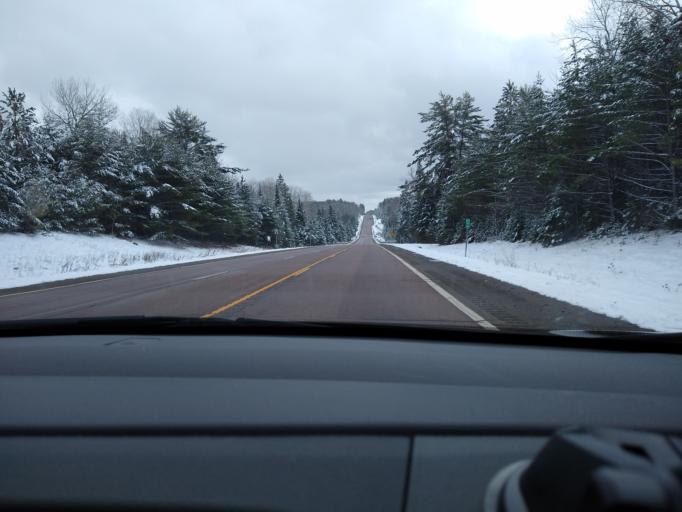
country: US
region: Wisconsin
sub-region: Vilas County
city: Eagle River
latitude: 46.1948
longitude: -89.0001
